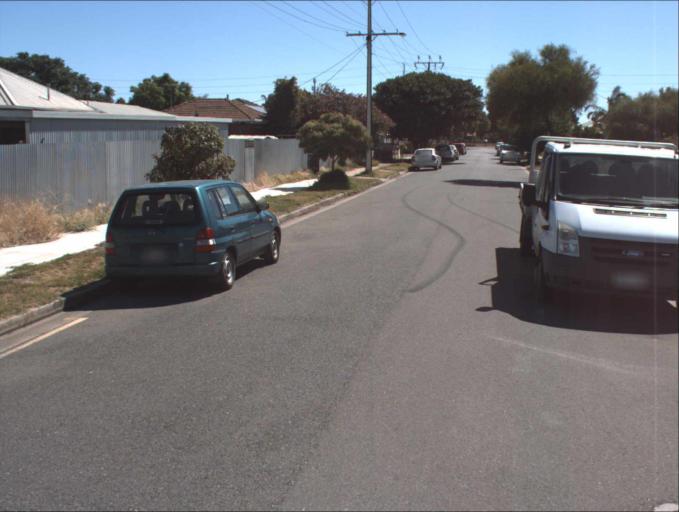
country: AU
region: South Australia
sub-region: Port Adelaide Enfield
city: Birkenhead
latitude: -34.8085
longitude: 138.5012
